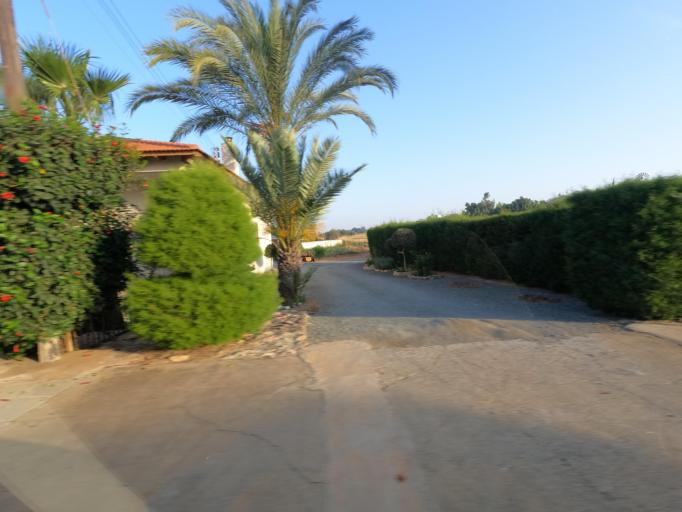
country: CY
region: Ammochostos
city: Frenaros
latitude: 35.0222
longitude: 33.9468
